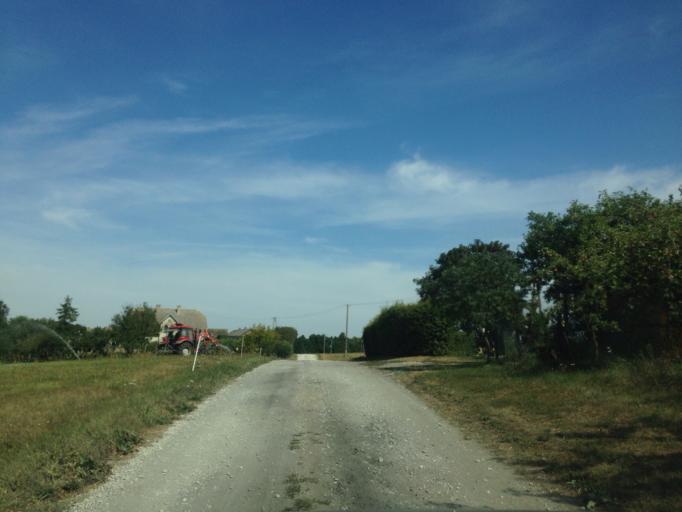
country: PL
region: Kujawsko-Pomorskie
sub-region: Powiat brodnicki
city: Bartniczka
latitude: 53.2325
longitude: 19.5666
